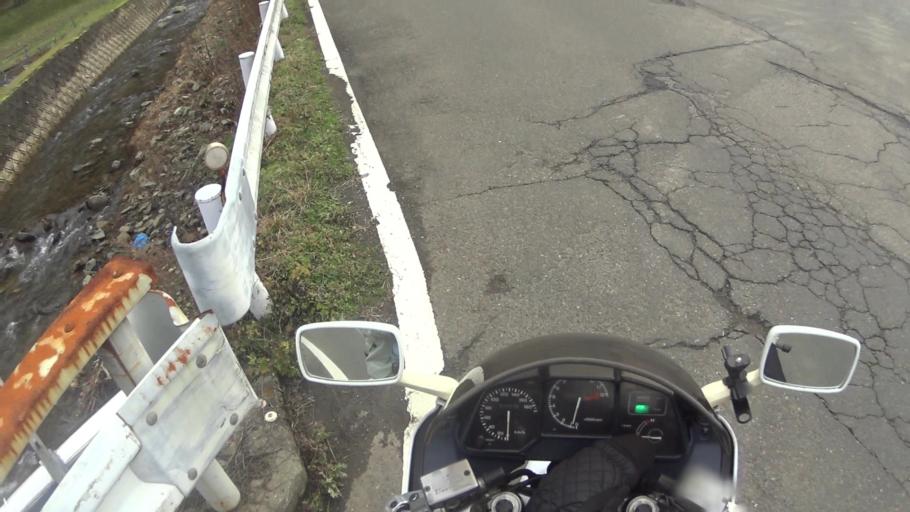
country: JP
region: Kyoto
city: Maizuru
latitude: 35.4255
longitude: 135.2978
